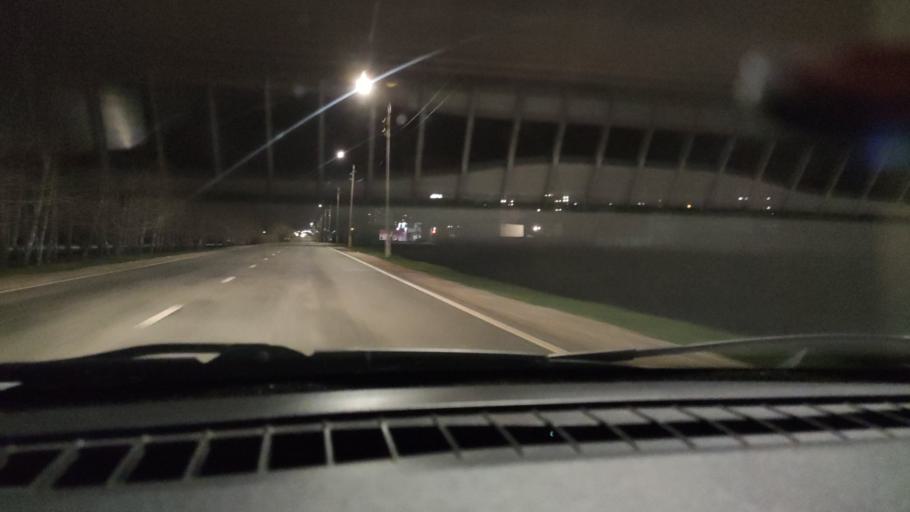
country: RU
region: Bashkortostan
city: Sterlitamak
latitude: 53.6445
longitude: 55.8903
